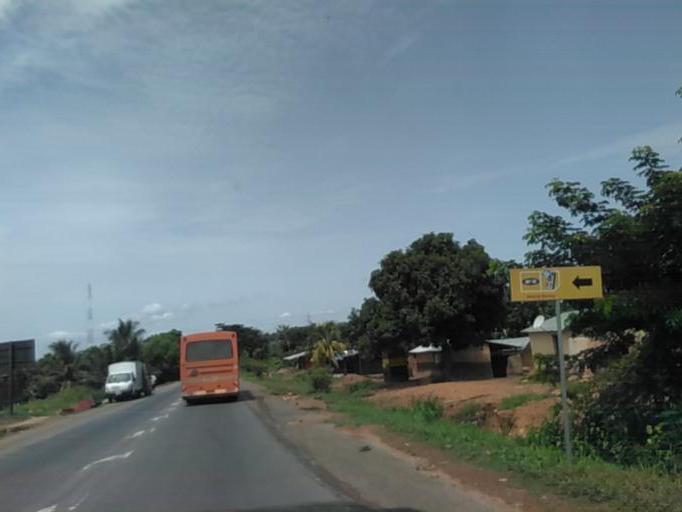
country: GH
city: Akropong
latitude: 6.1977
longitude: 0.0773
